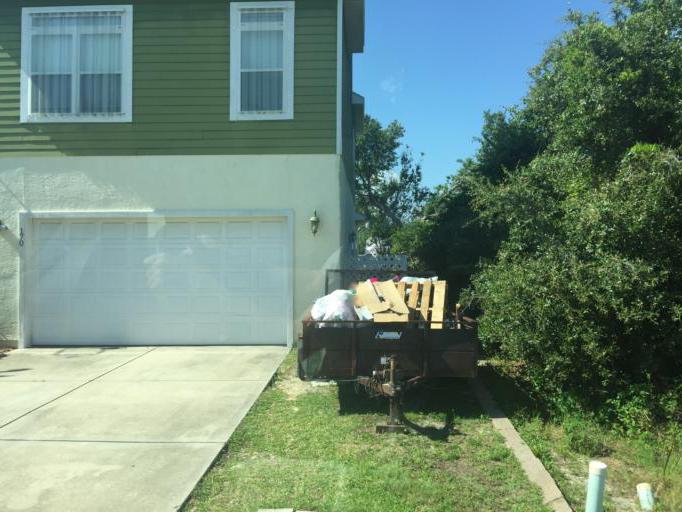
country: US
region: Florida
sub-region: Bay County
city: Panama City Beach
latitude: 30.2054
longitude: -85.8473
